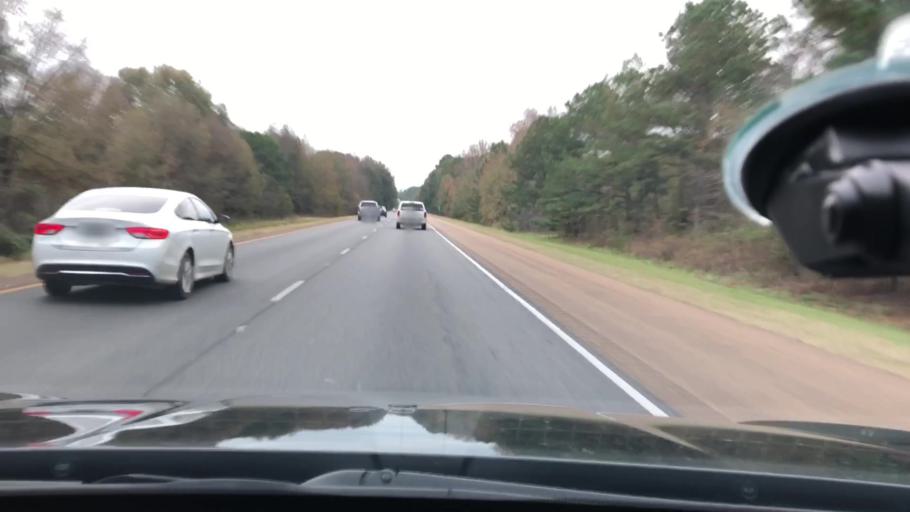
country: US
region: Arkansas
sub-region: Nevada County
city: Prescott
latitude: 33.8682
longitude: -93.3442
